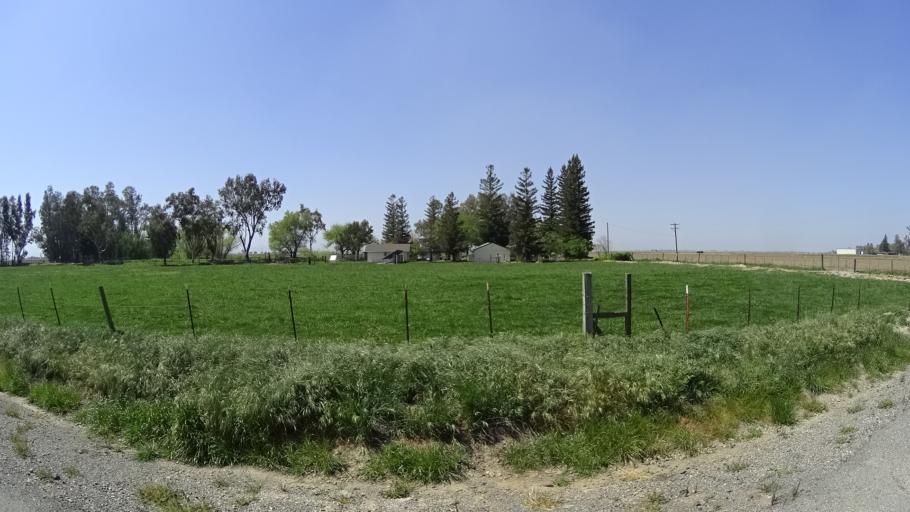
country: US
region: California
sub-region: Glenn County
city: Willows
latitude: 39.5433
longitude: -122.0980
